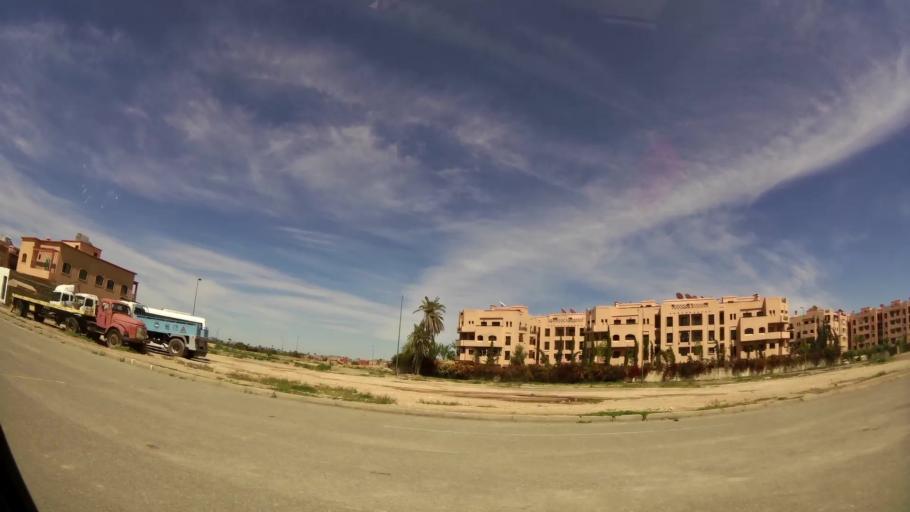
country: MA
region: Marrakech-Tensift-Al Haouz
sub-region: Marrakech
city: Marrakesh
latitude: 31.6631
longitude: -7.9915
